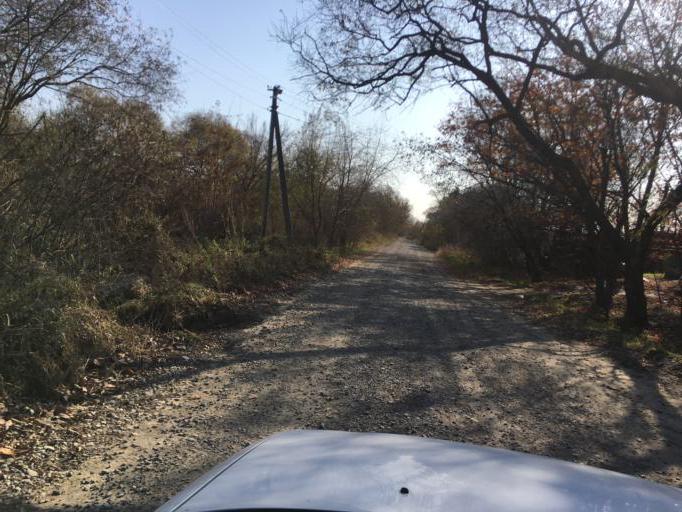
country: RU
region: Primorskiy
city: Dal'nerechensk
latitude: 45.9177
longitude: 133.7158
